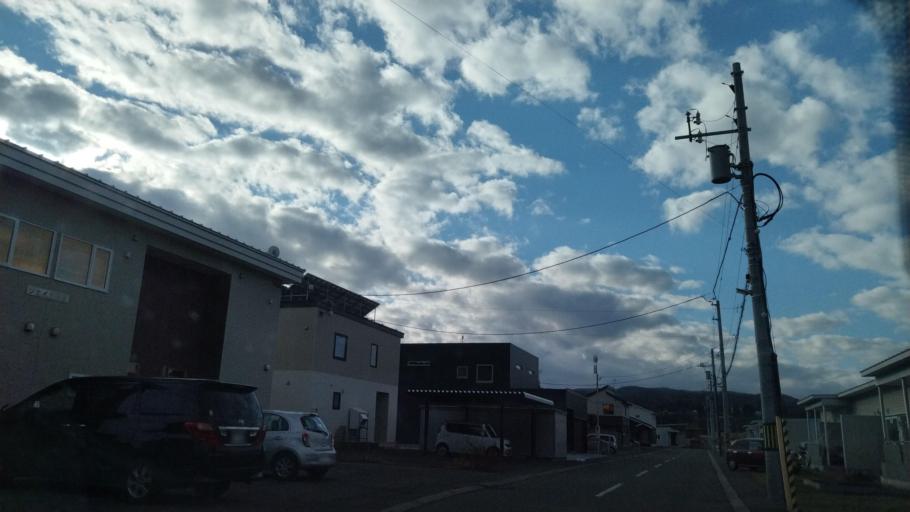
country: JP
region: Hokkaido
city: Otofuke
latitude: 43.2478
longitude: 143.5522
